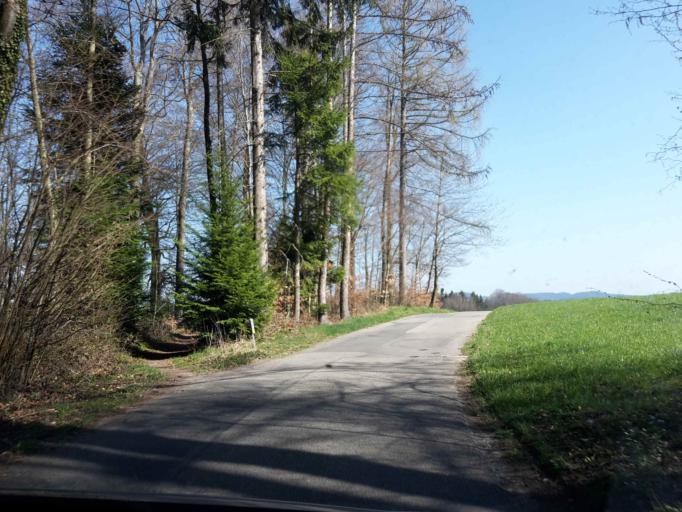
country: CH
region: Bern
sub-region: Oberaargau
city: Herzogenbuchsee
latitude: 47.1949
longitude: 7.7455
